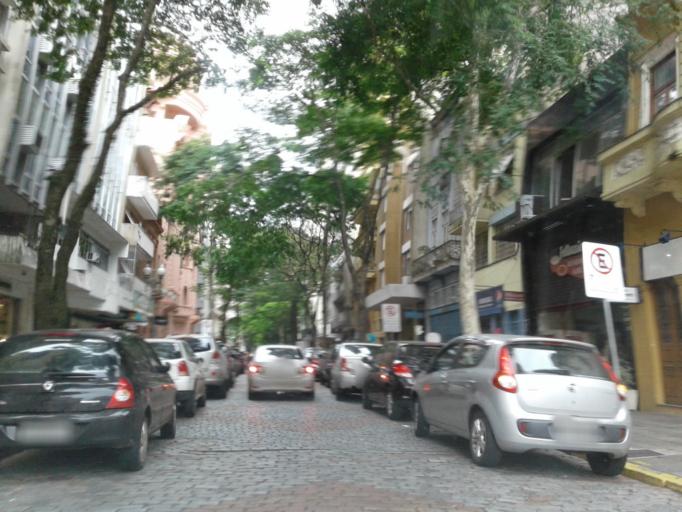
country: BR
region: Rio Grande do Sul
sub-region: Porto Alegre
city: Porto Alegre
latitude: -30.0318
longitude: -51.2350
